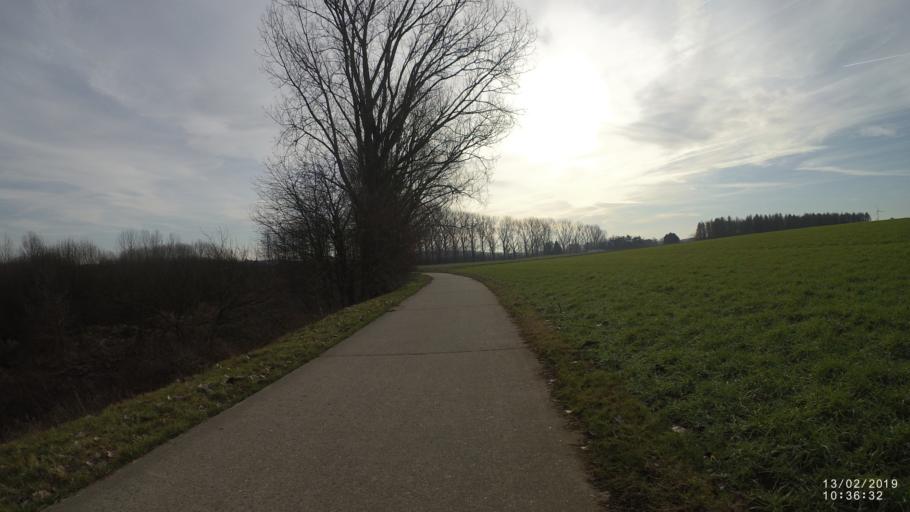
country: BE
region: Flanders
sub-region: Provincie Vlaams-Brabant
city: Diest
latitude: 50.9794
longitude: 5.0683
